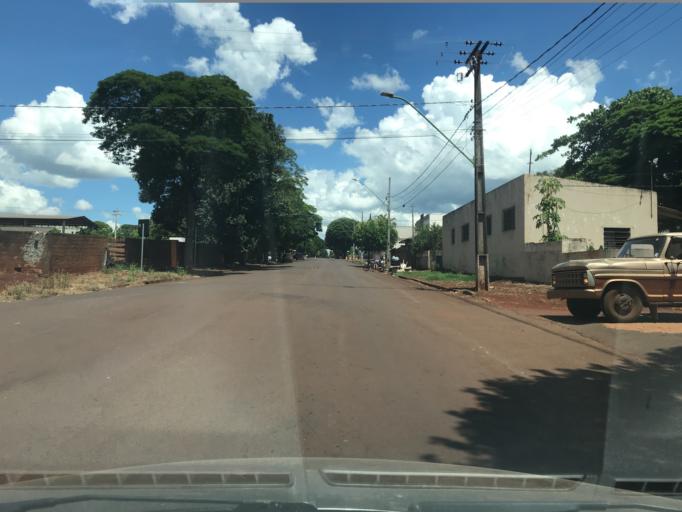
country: BR
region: Parana
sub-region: Palotina
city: Palotina
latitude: -24.2837
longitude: -53.8473
